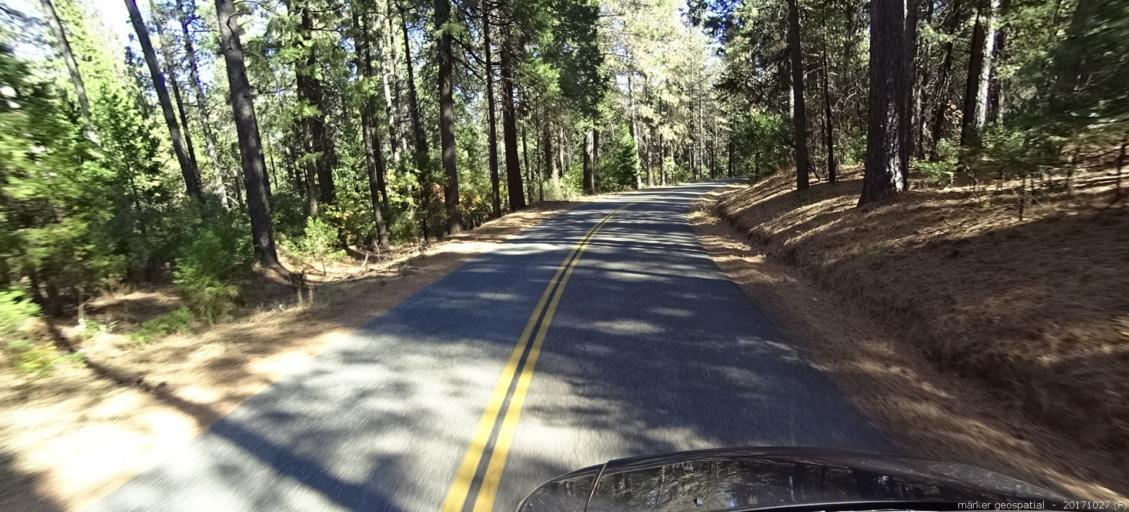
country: US
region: California
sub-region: Shasta County
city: Shingletown
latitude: 40.7176
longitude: -121.9914
